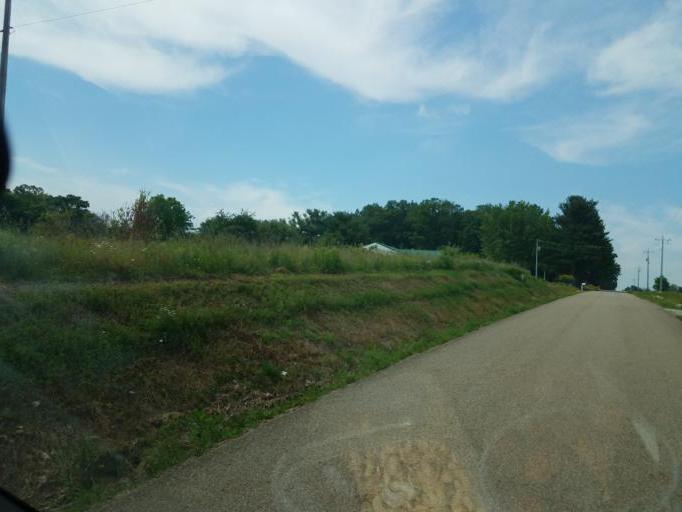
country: US
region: Ohio
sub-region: Knox County
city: Oak Hill
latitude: 40.2769
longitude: -82.2426
